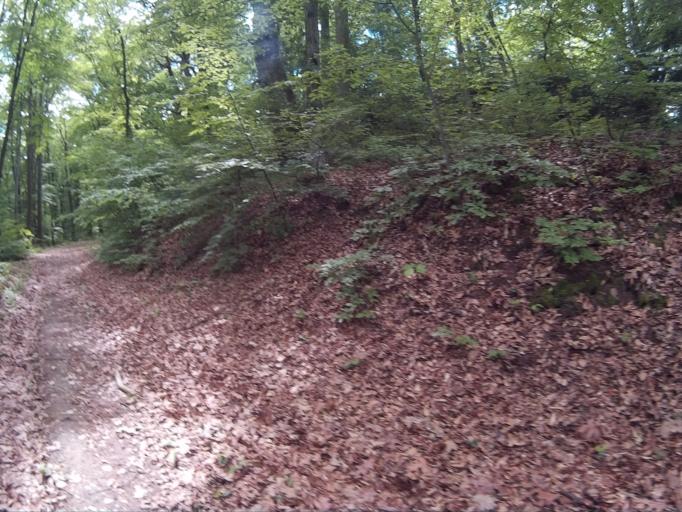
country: HU
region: Vas
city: Kormend
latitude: 46.9602
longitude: 16.5410
